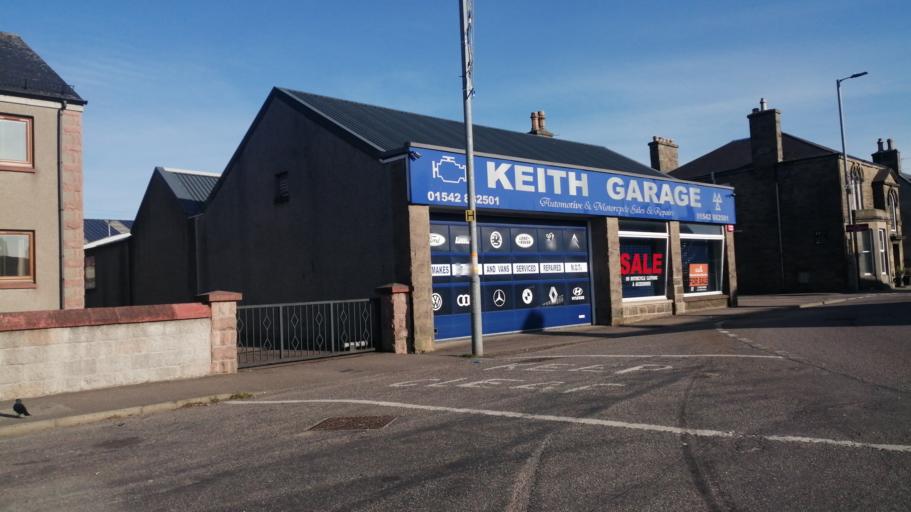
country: GB
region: Scotland
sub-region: Moray
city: Keith
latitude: 57.5428
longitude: -2.9480
